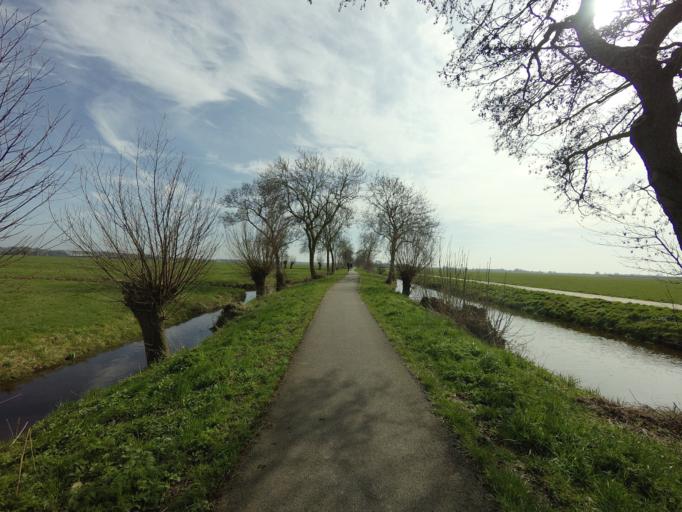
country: NL
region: South Holland
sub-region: Bodegraven-Reeuwijk
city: Bodegraven
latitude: 52.0907
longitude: 4.7102
